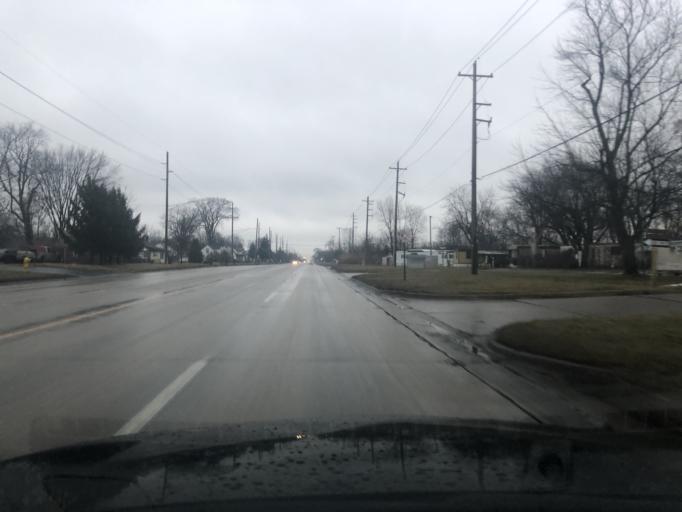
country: US
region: Michigan
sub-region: Wayne County
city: Inkster
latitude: 42.2680
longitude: -83.3190
